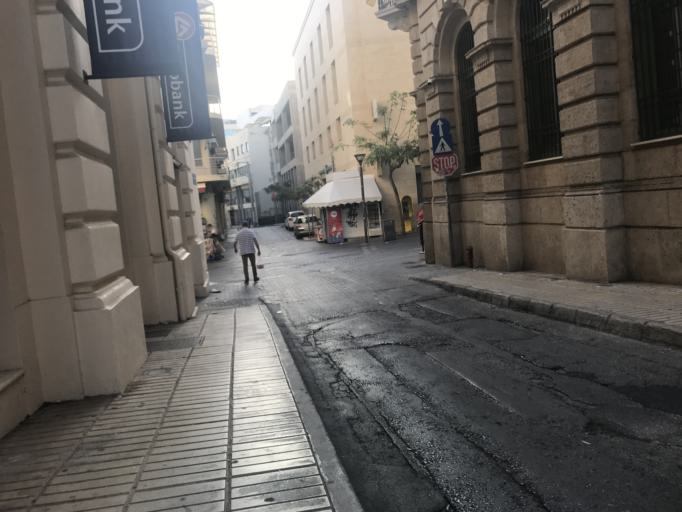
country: GR
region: Crete
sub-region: Nomos Irakleiou
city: Irakleion
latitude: 35.3408
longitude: 25.1334
